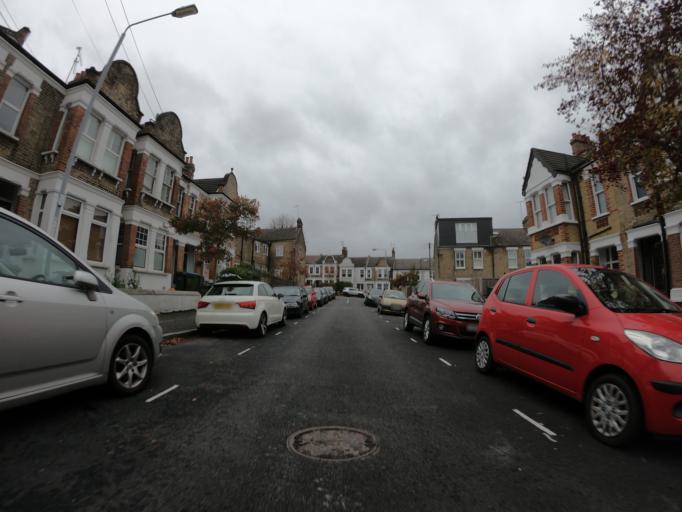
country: GB
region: England
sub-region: Greater London
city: Blackheath
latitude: 51.4820
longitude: 0.0237
